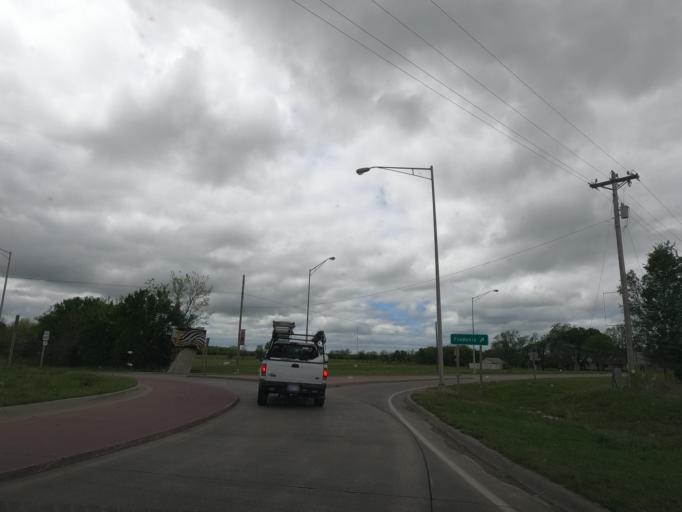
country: US
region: Kansas
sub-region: Wilson County
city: Fredonia
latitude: 37.5302
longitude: -95.8019
